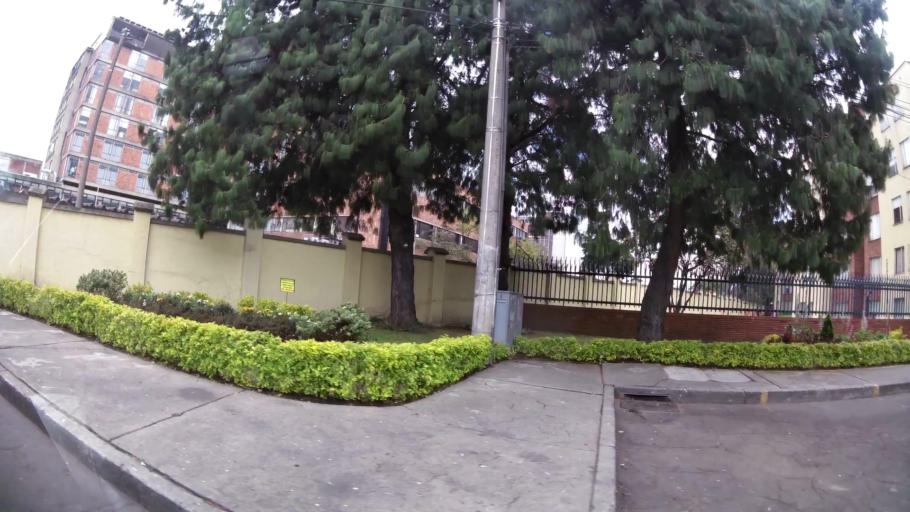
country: CO
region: Bogota D.C.
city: Bogota
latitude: 4.6225
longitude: -74.0825
